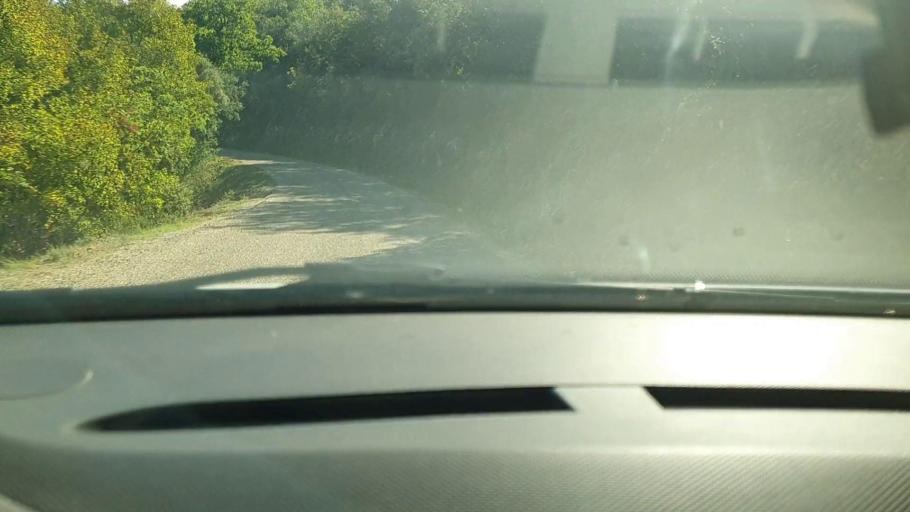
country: FR
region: Languedoc-Roussillon
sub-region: Departement du Gard
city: Saint-Ambroix
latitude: 44.2149
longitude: 4.2953
